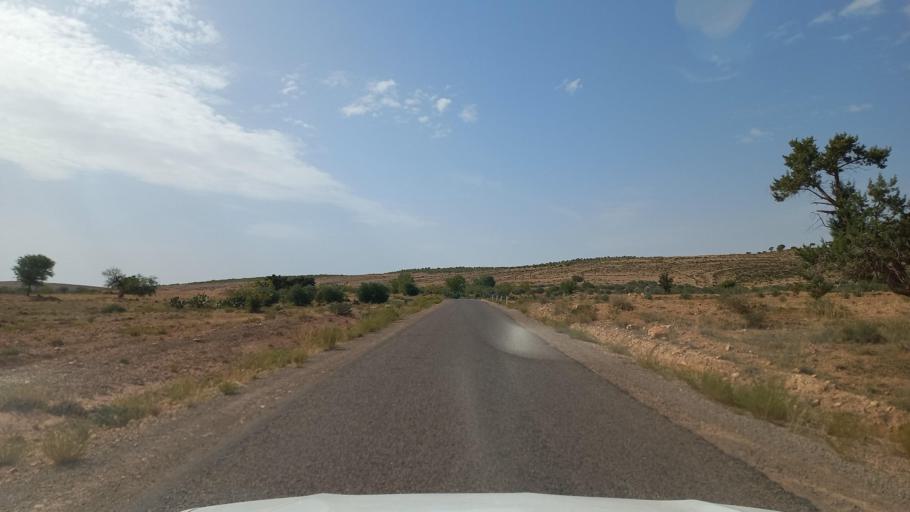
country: TN
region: Al Qasrayn
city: Kasserine
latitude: 35.3677
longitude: 8.8678
